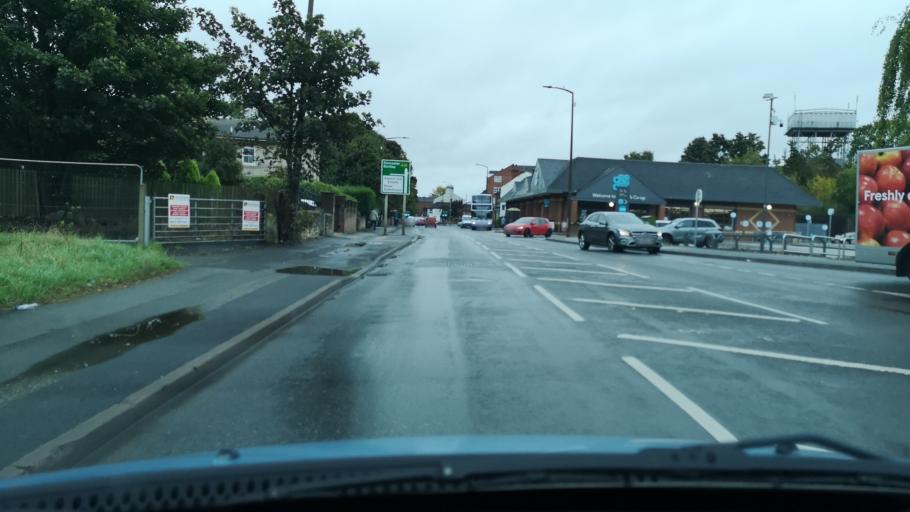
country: GB
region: England
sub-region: Doncaster
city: Askern
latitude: 53.6180
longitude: -1.1532
